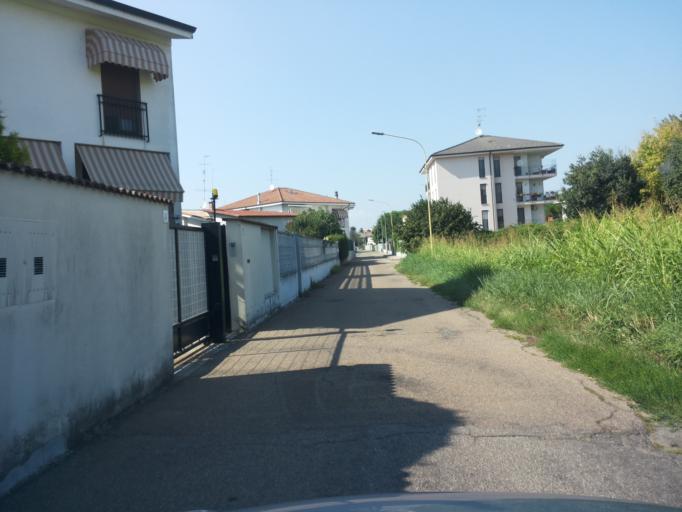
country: IT
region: Piedmont
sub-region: Provincia di Vercelli
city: Vercelli
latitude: 45.3120
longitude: 8.4317
